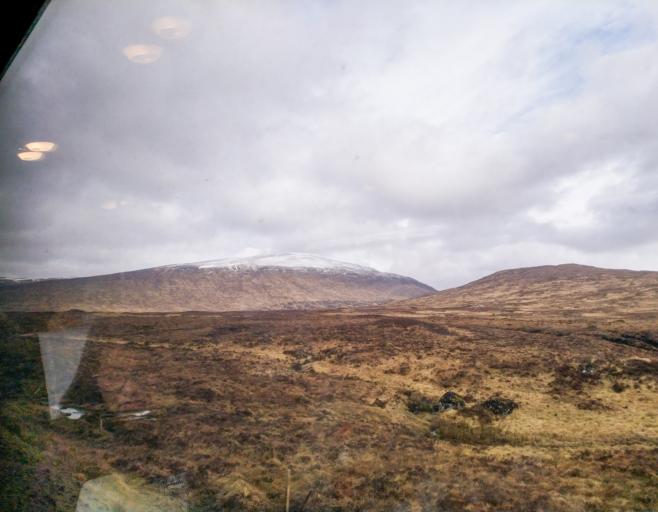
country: GB
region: Scotland
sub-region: Highland
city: Spean Bridge
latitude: 56.7455
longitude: -4.6708
